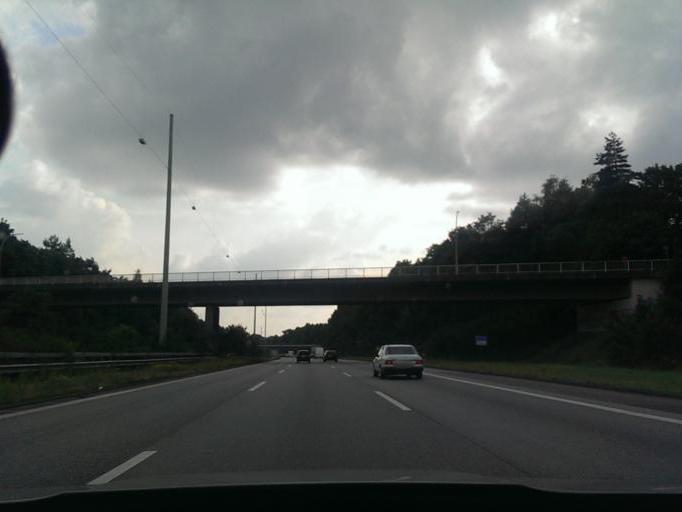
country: DE
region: Hamburg
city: Stellingen
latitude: 53.5730
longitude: 9.9040
